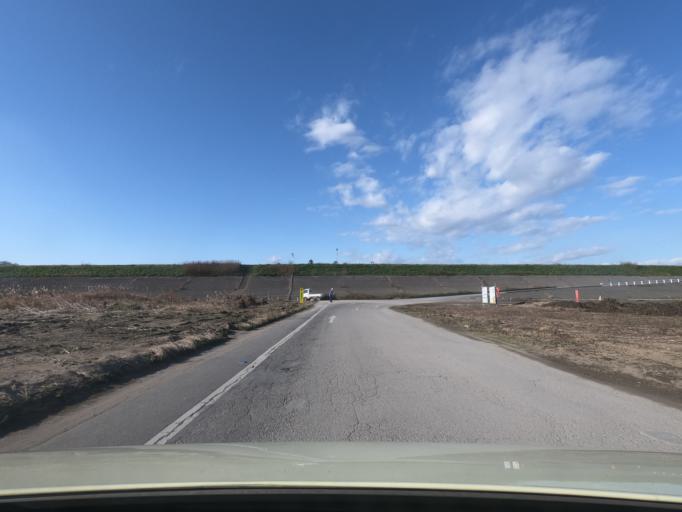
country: JP
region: Ibaraki
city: Koga
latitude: 36.2467
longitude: 139.7327
